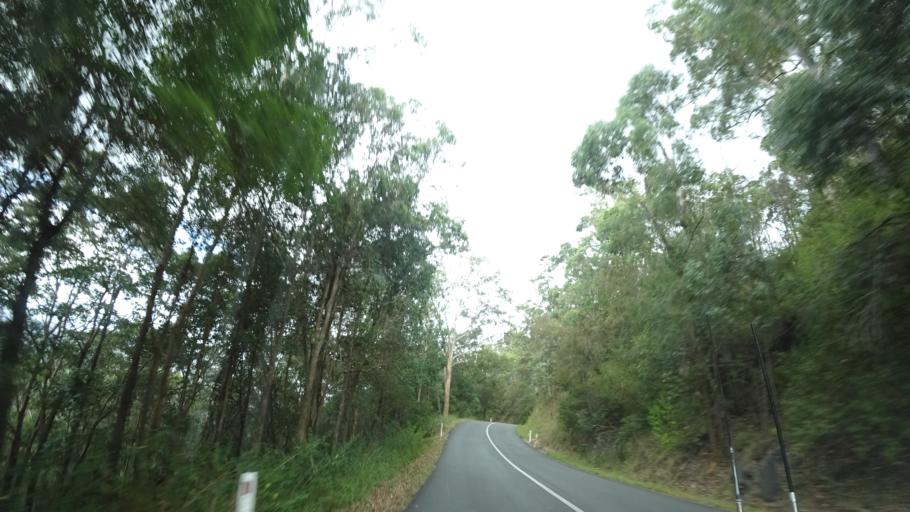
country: AU
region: Queensland
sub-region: Moreton Bay
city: Highvale
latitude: -27.3984
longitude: 152.8106
